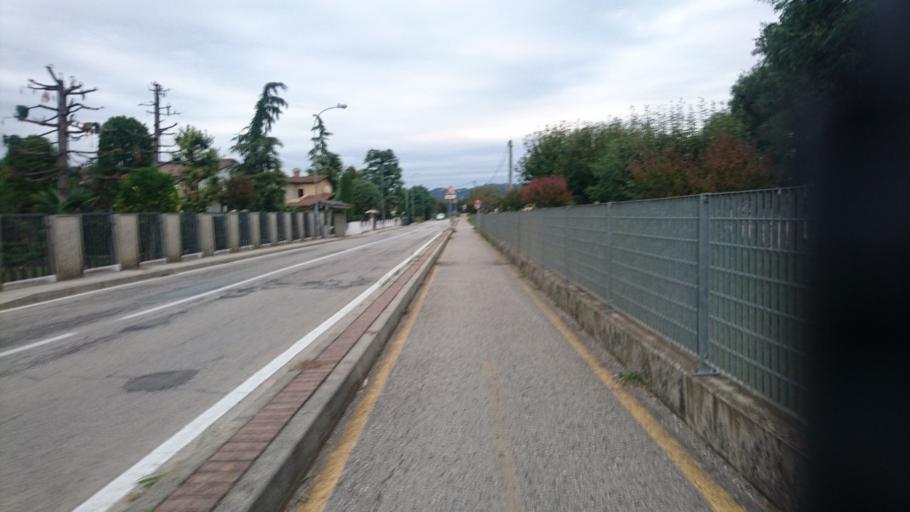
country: IT
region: Veneto
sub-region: Provincia di Vicenza
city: Sovizzo
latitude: 45.5179
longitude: 11.4321
